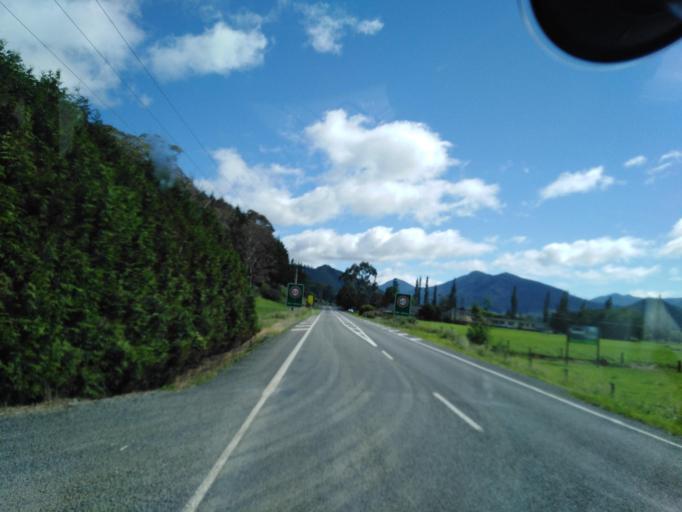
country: NZ
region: Nelson
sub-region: Nelson City
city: Nelson
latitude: -41.2364
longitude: 173.5803
